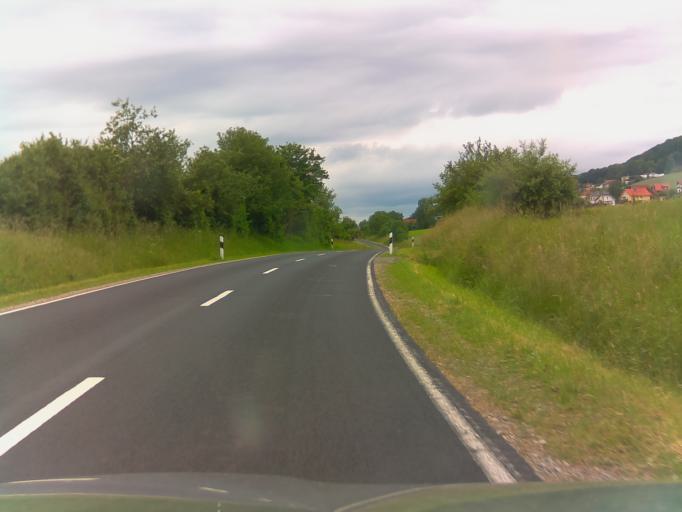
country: DE
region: Bavaria
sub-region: Regierungsbezirk Unterfranken
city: Schondra
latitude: 50.2930
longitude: 9.8410
